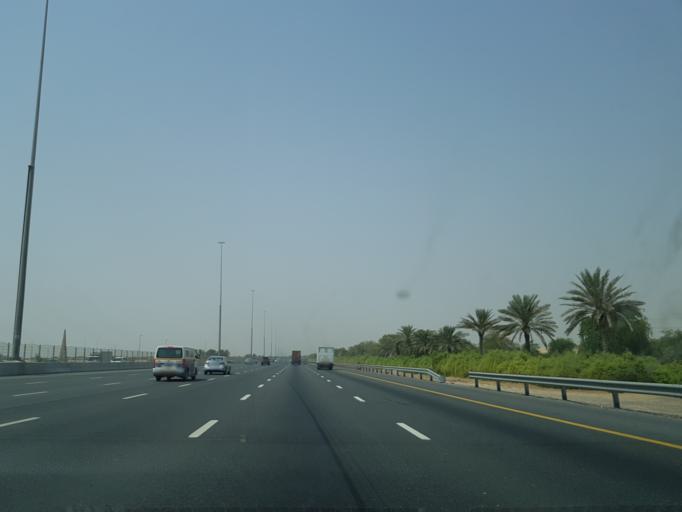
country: AE
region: Dubai
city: Dubai
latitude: 25.0712
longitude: 55.3011
